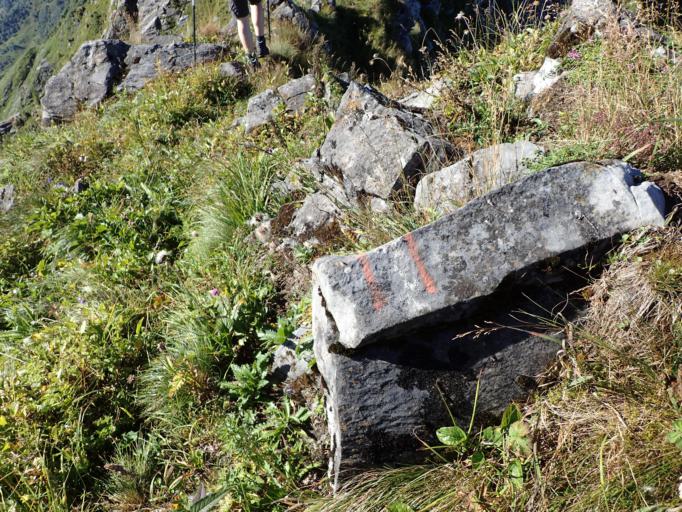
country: AT
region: Salzburg
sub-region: Politischer Bezirk Zell am See
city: Taxenbach
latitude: 47.2464
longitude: 12.9036
